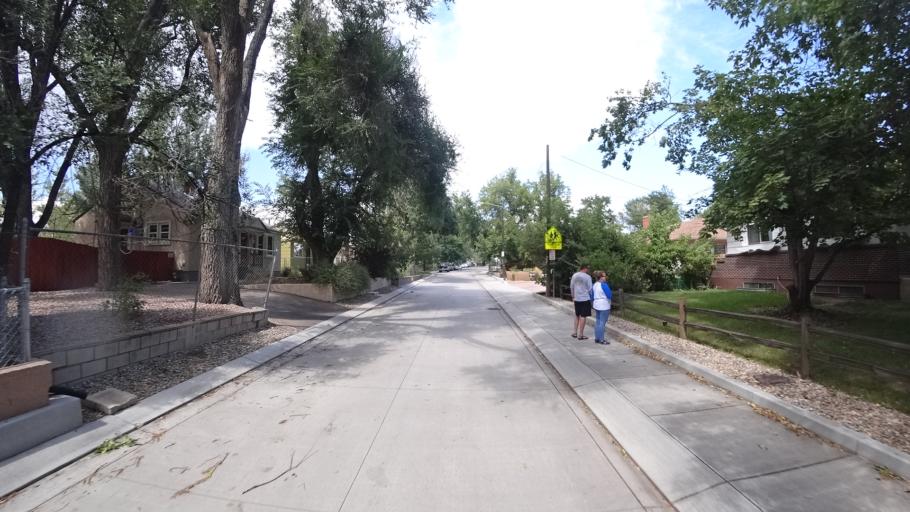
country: US
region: Colorado
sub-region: El Paso County
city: Colorado Springs
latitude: 38.8522
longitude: -104.8089
